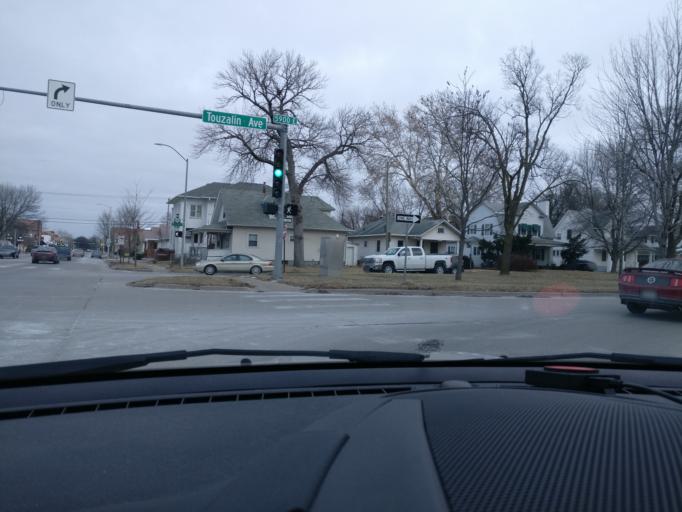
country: US
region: Nebraska
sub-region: Lancaster County
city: Lincoln
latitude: 40.8571
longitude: -96.6403
